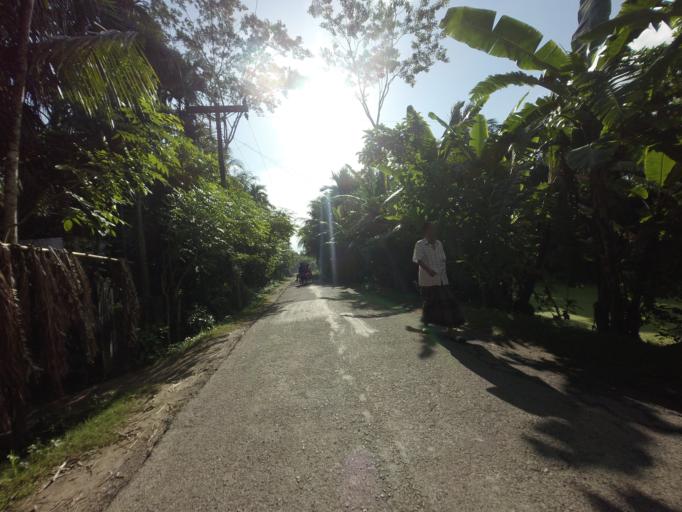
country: BD
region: Khulna
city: Kalia
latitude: 23.0146
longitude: 89.5970
